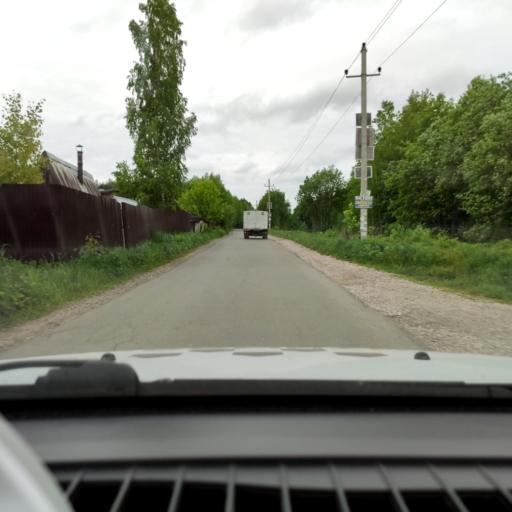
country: RU
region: Perm
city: Novyye Lyady
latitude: 58.0459
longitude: 56.6382
